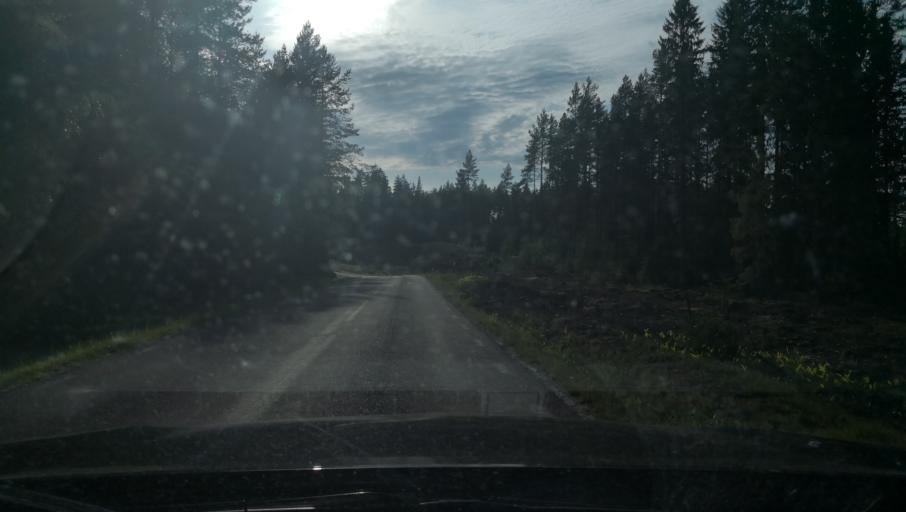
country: SE
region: Dalarna
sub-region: Smedjebackens Kommun
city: Smedjebacken
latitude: 60.0403
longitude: 15.3121
